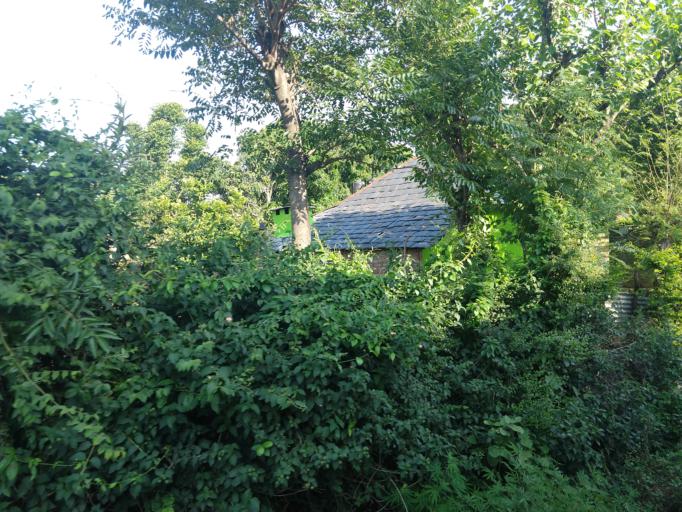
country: IN
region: Himachal Pradesh
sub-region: Chamba
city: Chowari
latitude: 32.3675
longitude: 75.9212
